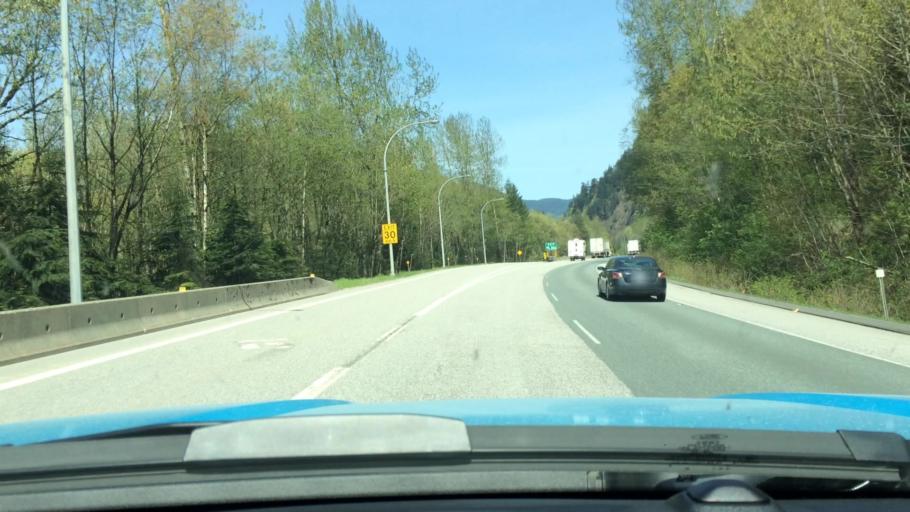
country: CA
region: British Columbia
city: Agassiz
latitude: 49.2543
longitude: -121.6788
